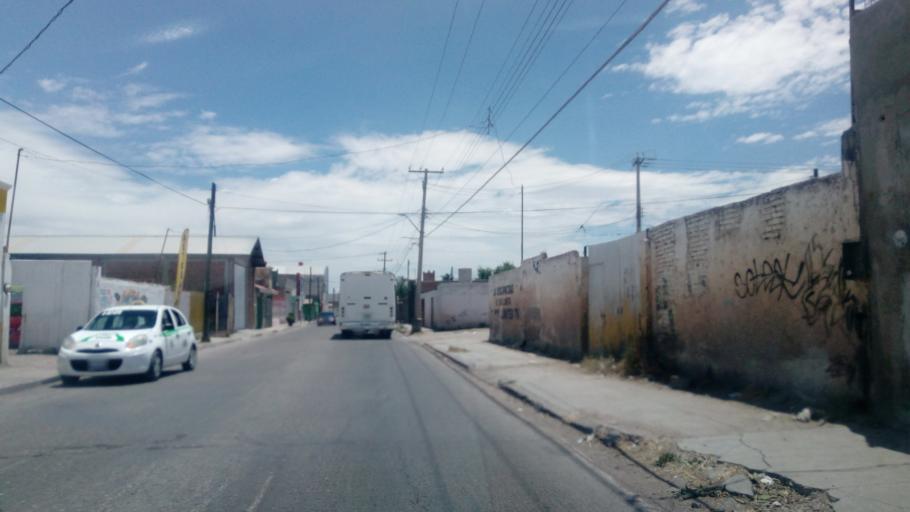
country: MX
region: Durango
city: Victoria de Durango
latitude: 24.0133
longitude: -104.6374
